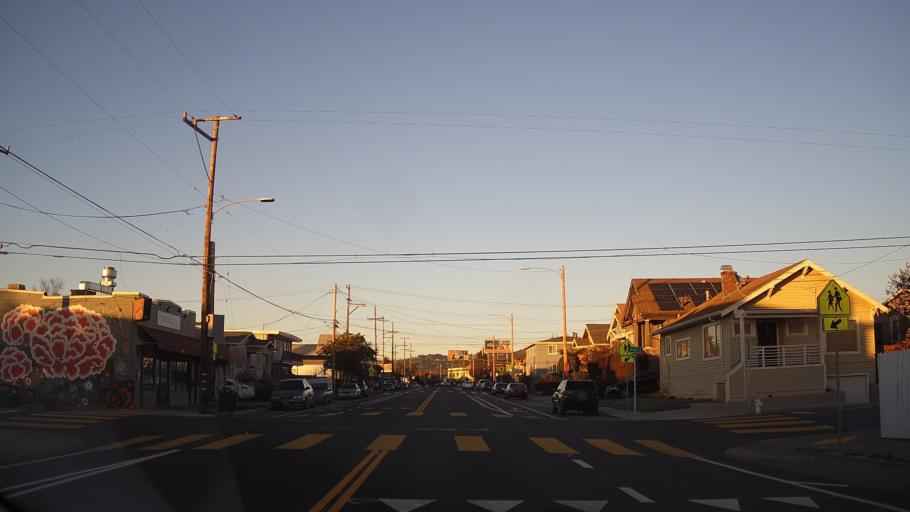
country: US
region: California
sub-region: Alameda County
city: Emeryville
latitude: 37.8321
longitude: -122.2736
